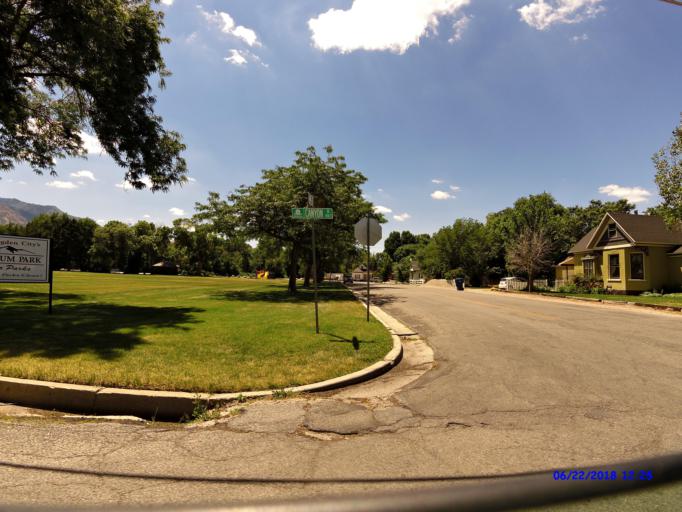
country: US
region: Utah
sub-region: Weber County
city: Ogden
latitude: 41.2377
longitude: -111.9652
